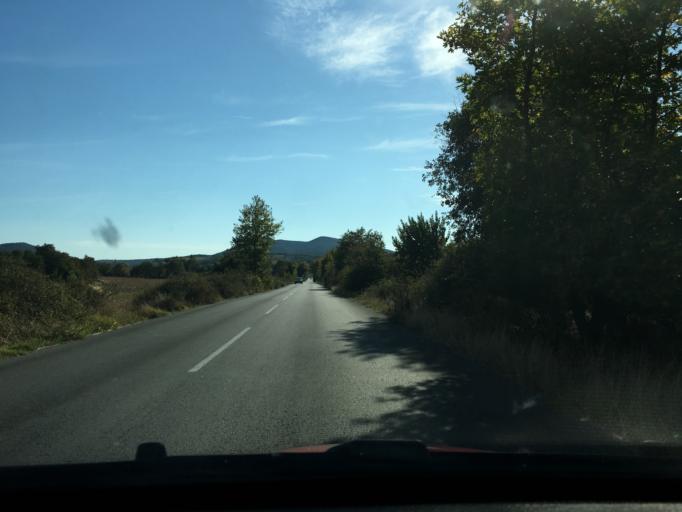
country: GR
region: Central Macedonia
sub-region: Nomos Chalkidikis
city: Megali Panagia
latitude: 40.3757
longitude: 23.6956
